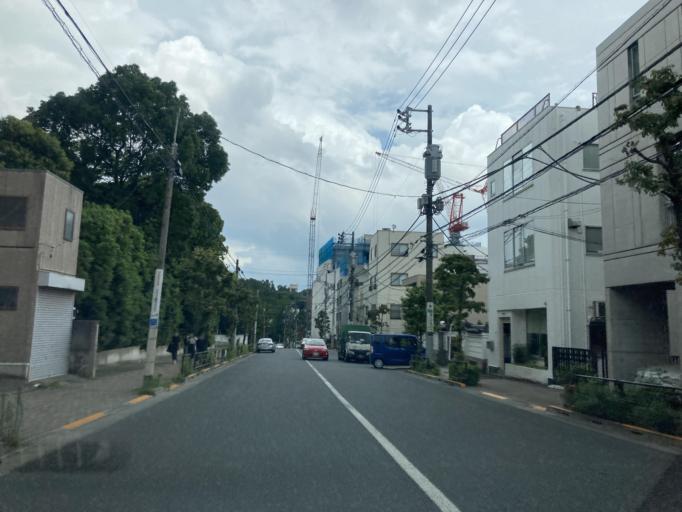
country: JP
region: Tokyo
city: Tokyo
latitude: 35.7158
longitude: 139.7430
